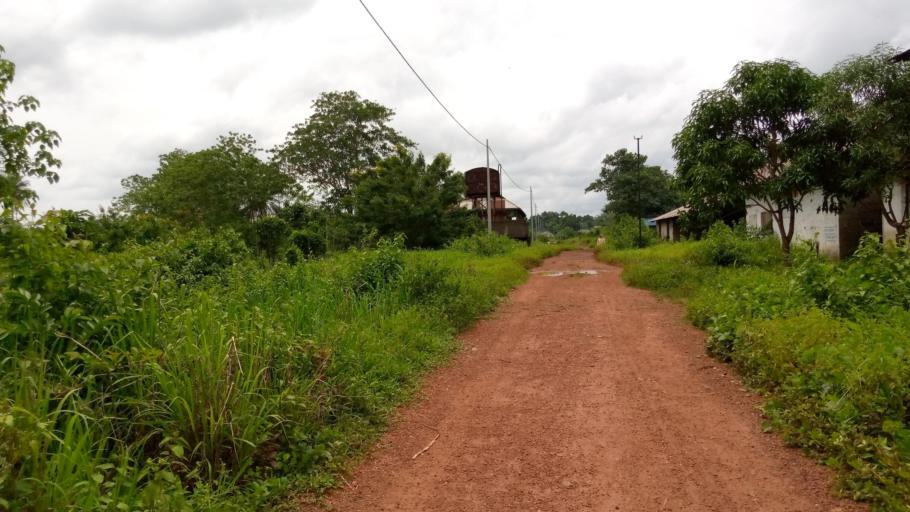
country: SL
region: Southern Province
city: Rotifunk
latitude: 8.1899
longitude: -12.5730
